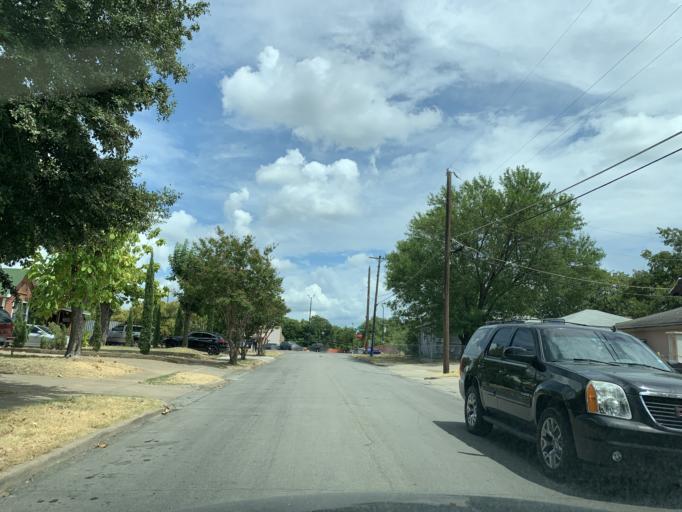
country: US
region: Texas
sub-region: Dallas County
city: Cockrell Hill
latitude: 32.7331
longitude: -96.8752
